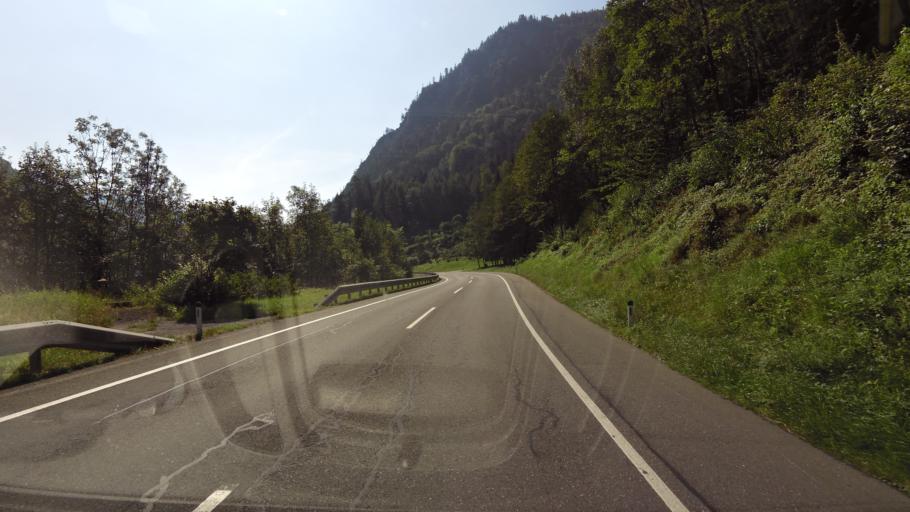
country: AT
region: Salzburg
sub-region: Politischer Bezirk Sankt Johann im Pongau
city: Werfen
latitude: 47.4910
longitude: 13.1770
